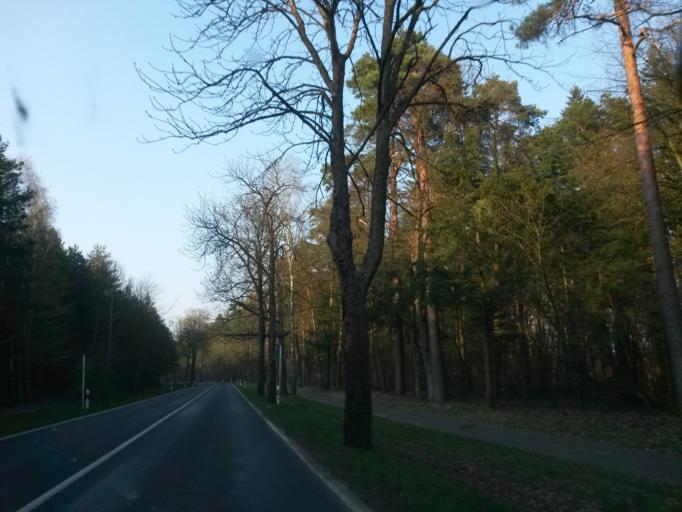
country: DE
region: Brandenburg
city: Grunheide
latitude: 52.4413
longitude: 13.8528
